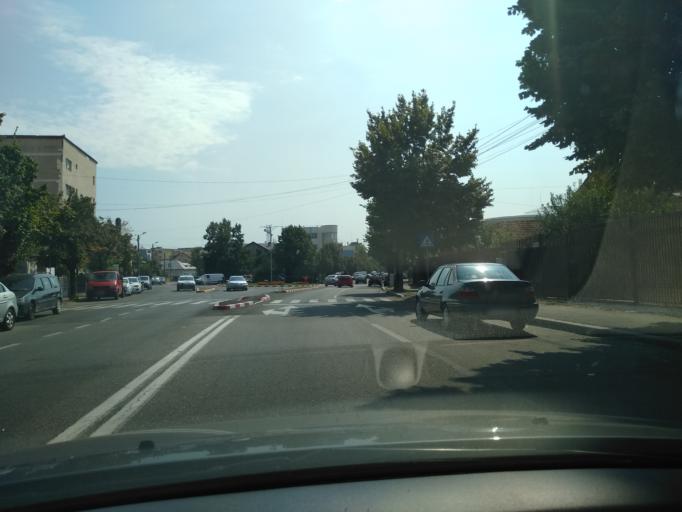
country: RO
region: Gorj
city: Targu Jiu
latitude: 45.0455
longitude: 23.2726
